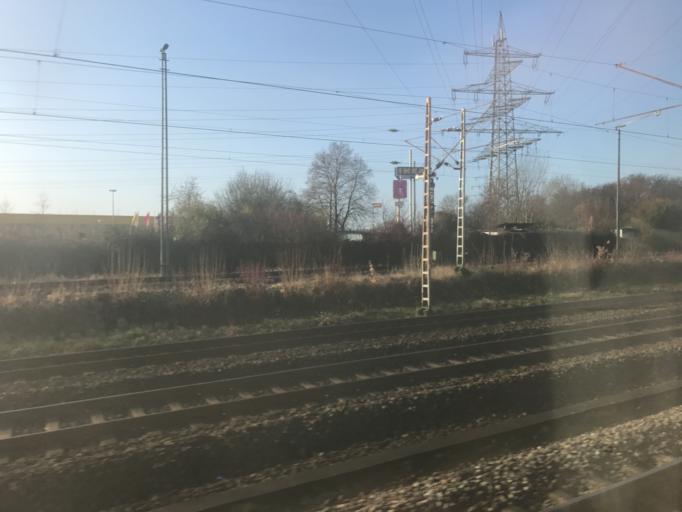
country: DE
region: North Rhine-Westphalia
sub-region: Regierungsbezirk Dusseldorf
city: Erkrath
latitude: 51.1893
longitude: 6.8515
